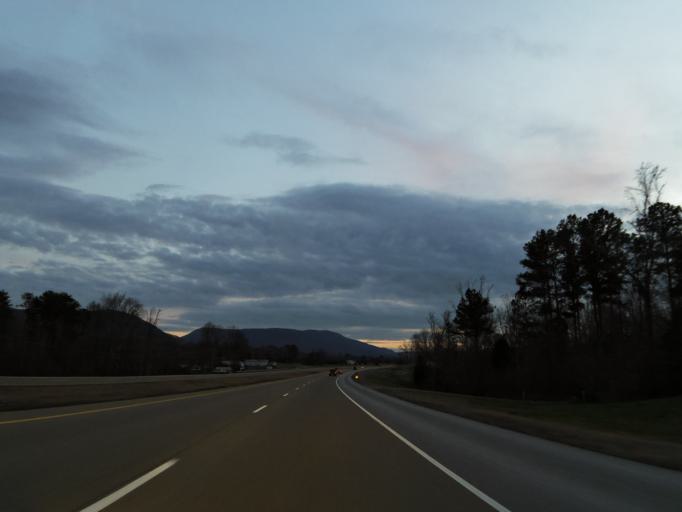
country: US
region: Tennessee
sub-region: McMinn County
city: Etowah
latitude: 35.2720
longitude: -84.5460
